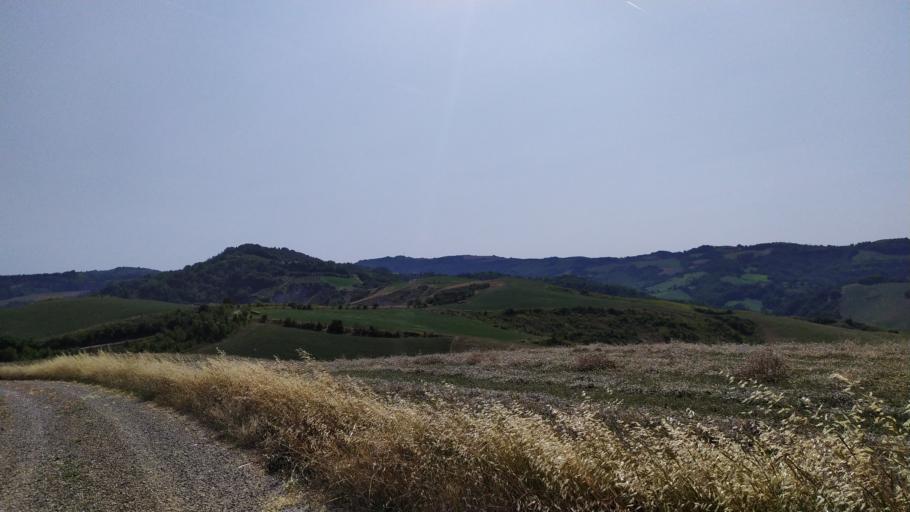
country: IT
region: Emilia-Romagna
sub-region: Forli-Cesena
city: Dovadola
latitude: 44.1655
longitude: 11.8971
